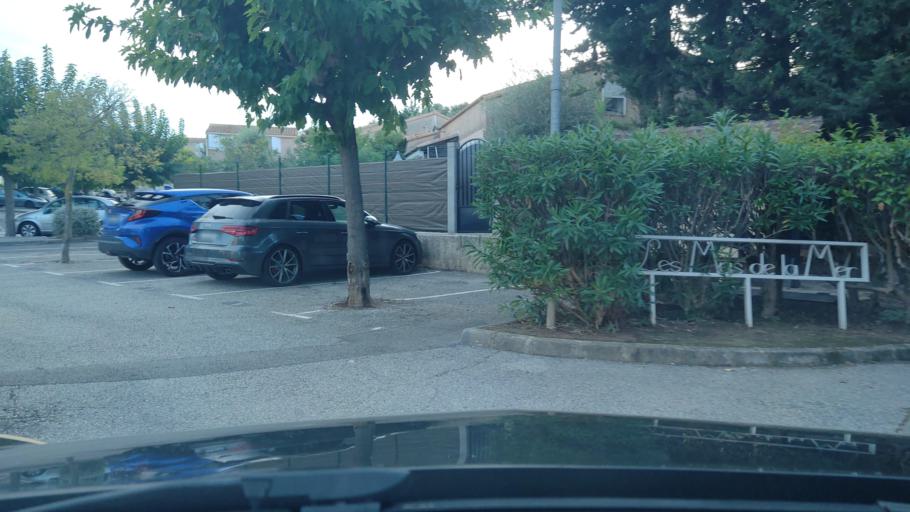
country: FR
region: Provence-Alpes-Cote d'Azur
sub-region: Departement du Var
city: Sanary-sur-Mer
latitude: 43.1273
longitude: 5.7941
